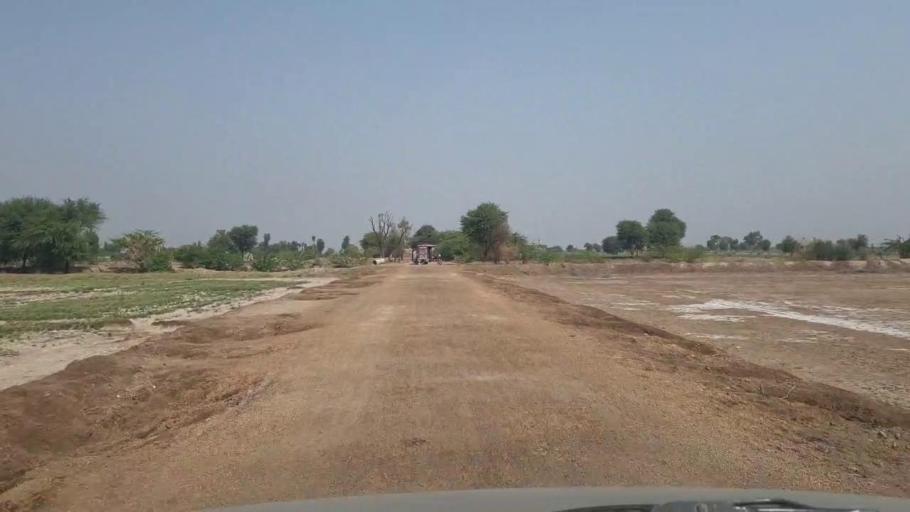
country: PK
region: Sindh
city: Chor
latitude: 25.4845
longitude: 69.7410
